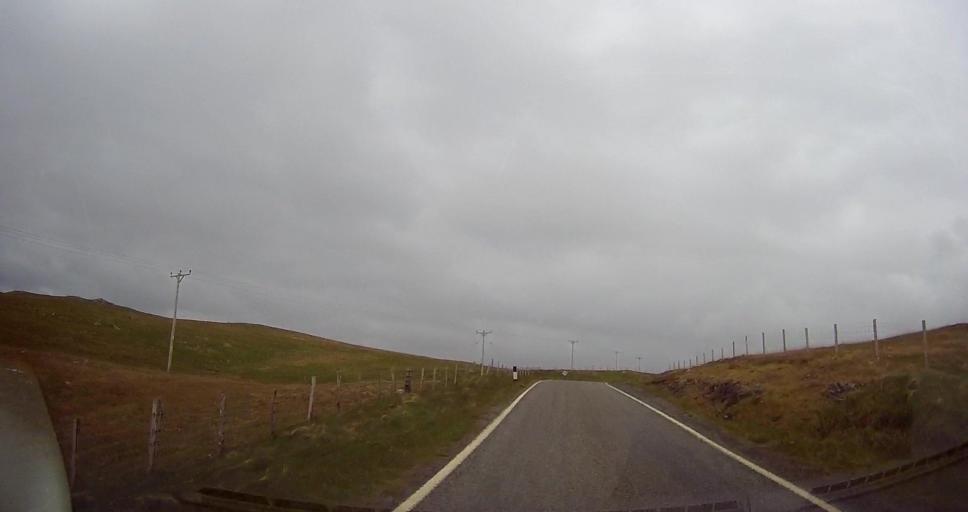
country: GB
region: Scotland
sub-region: Shetland Islands
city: Sandwick
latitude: 60.2374
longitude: -1.5428
